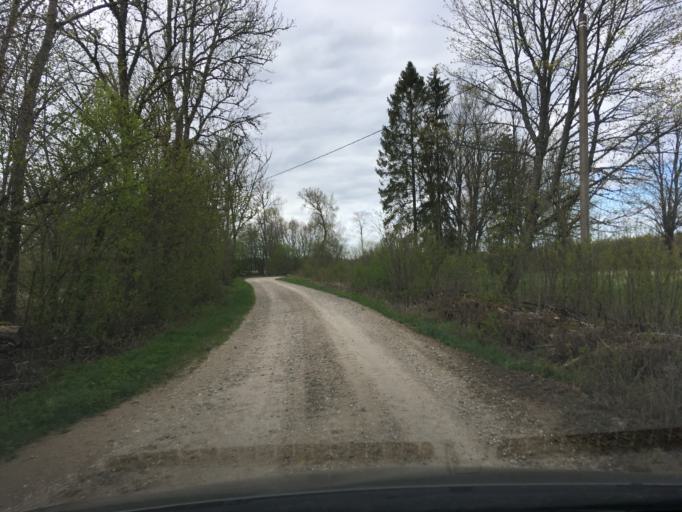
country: EE
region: Laeaene
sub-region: Lihula vald
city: Lihula
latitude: 58.5759
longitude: 23.7236
